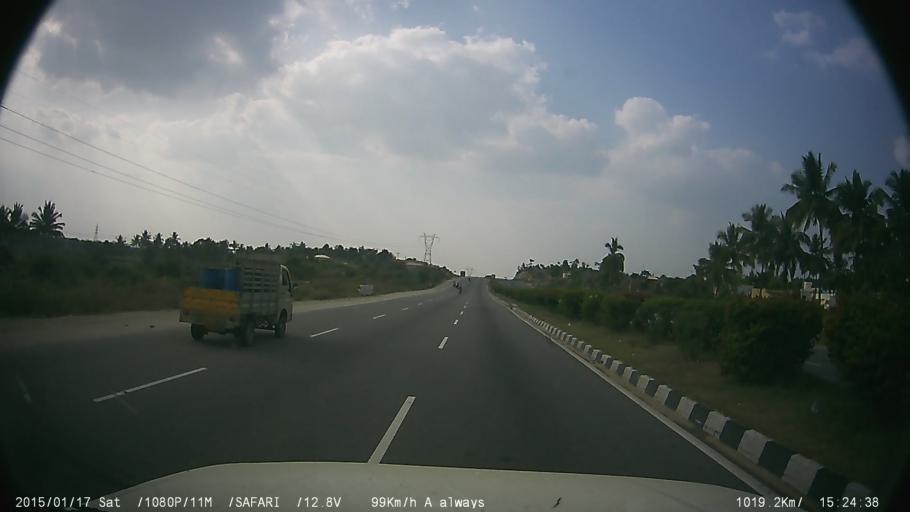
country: IN
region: Tamil Nadu
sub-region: Krishnagiri
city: Krishnagiri
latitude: 12.6081
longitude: 78.0977
